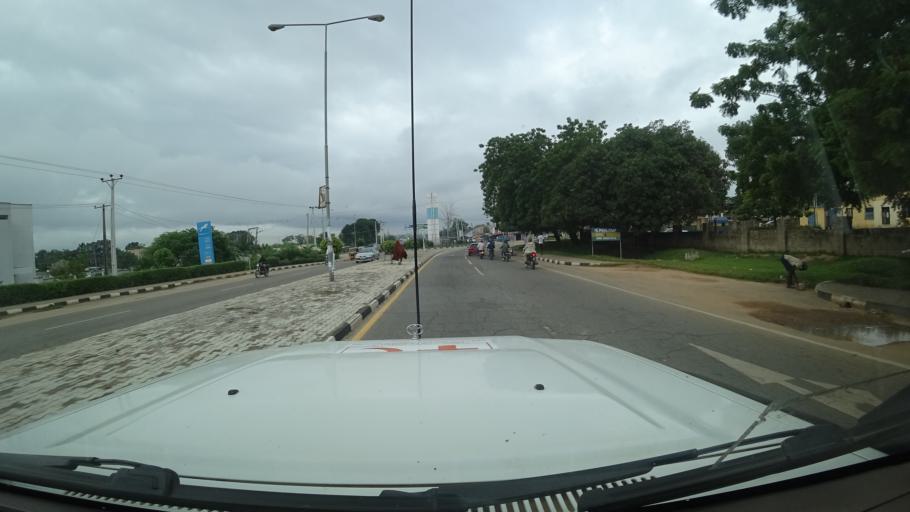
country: NG
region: Niger
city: Minna
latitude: 9.6103
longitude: 6.5515
